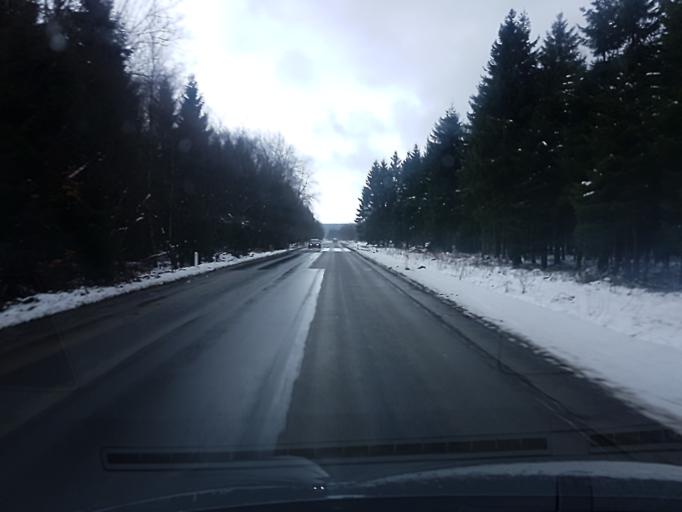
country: BE
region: Wallonia
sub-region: Province de Liege
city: Eupen
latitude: 50.5581
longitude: 6.0474
